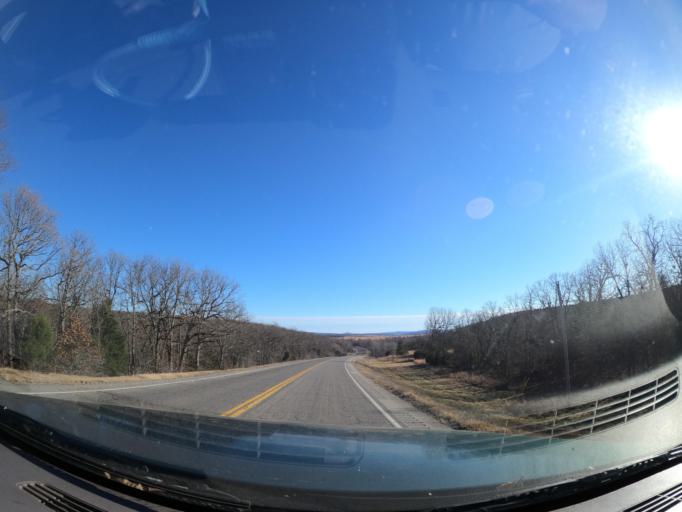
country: US
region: Oklahoma
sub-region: Pittsburg County
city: Longtown
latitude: 35.2224
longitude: -95.4297
